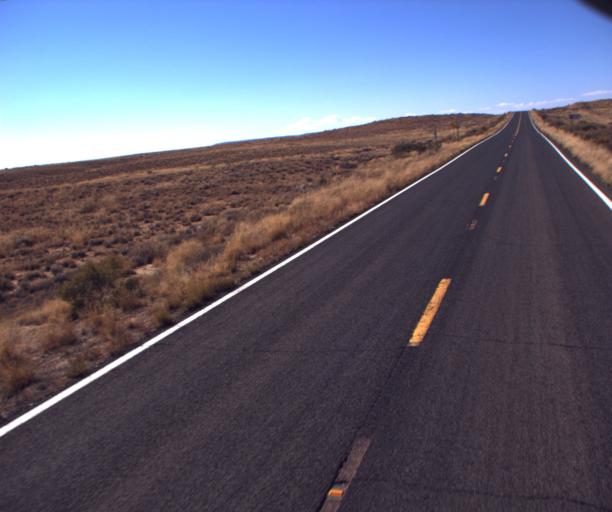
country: US
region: Arizona
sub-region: Navajo County
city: First Mesa
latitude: 35.9773
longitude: -110.7518
